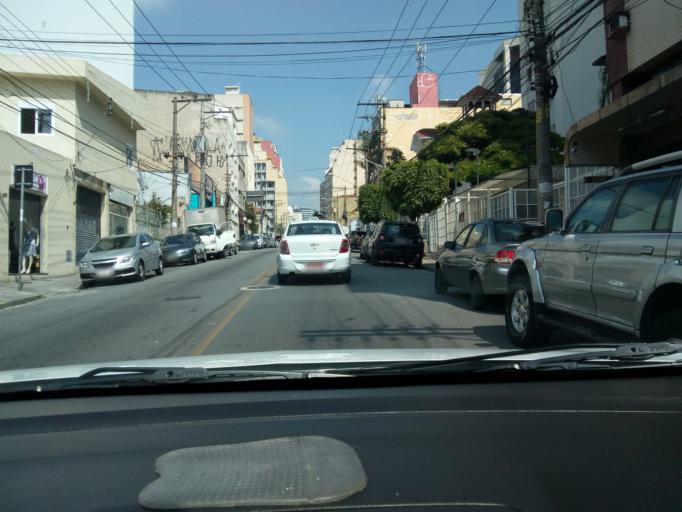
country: BR
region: Sao Paulo
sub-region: Sao Paulo
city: Sao Paulo
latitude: -23.5615
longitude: -46.6328
